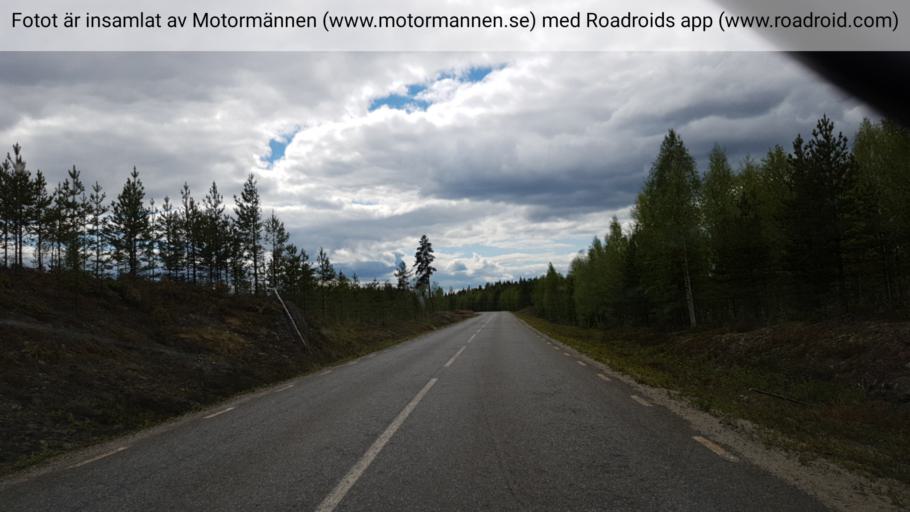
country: SE
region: Vaesterbotten
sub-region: Vindelns Kommun
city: Vindeln
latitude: 64.3883
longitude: 19.6741
